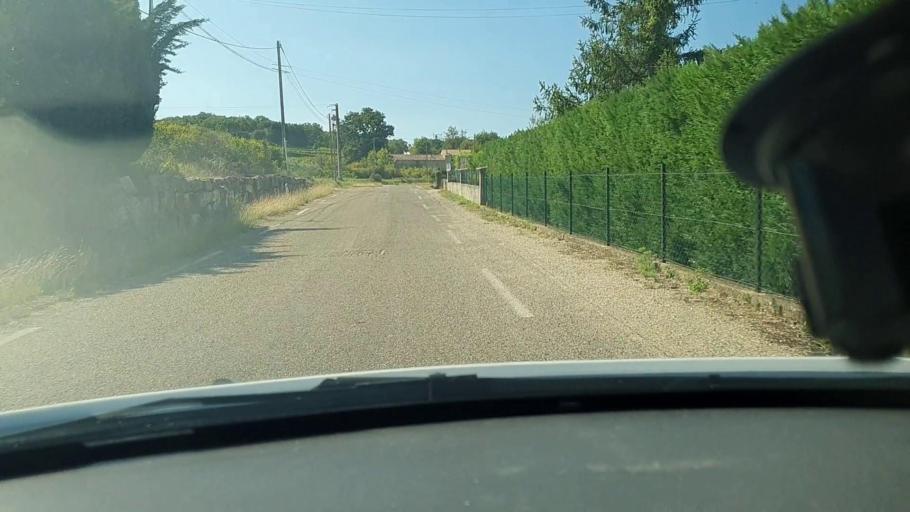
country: FR
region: Languedoc-Roussillon
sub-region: Departement du Gard
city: Saint-Paulet-de-Caisson
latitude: 44.2575
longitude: 4.5911
